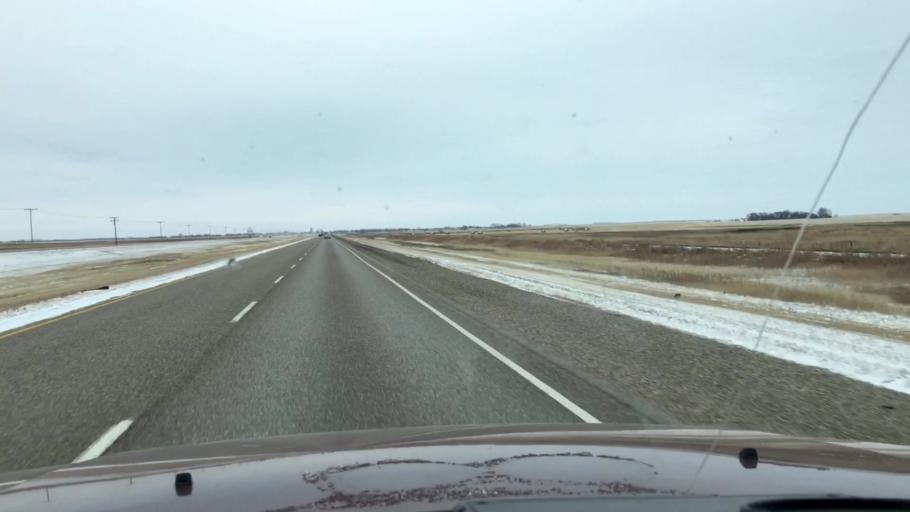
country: CA
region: Saskatchewan
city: Watrous
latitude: 51.0846
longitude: -105.8525
